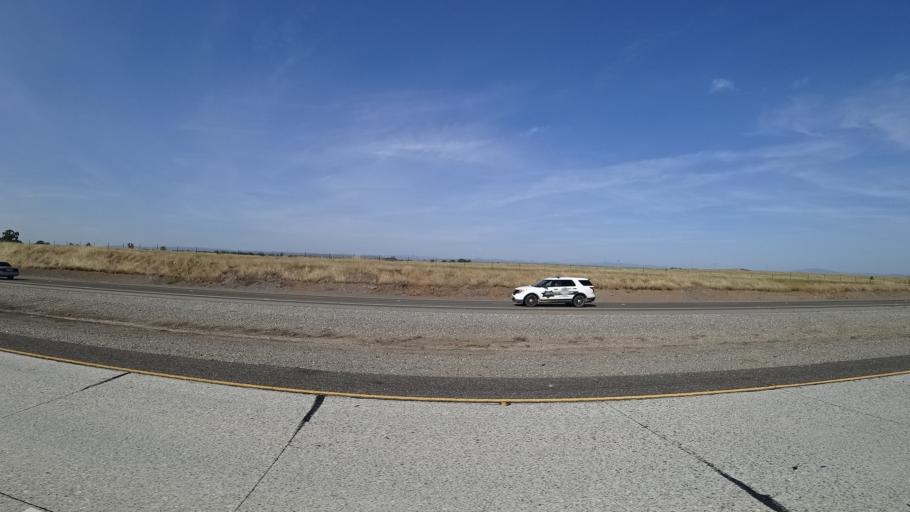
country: US
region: California
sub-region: Butte County
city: Durham
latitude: 39.6765
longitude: -121.7583
